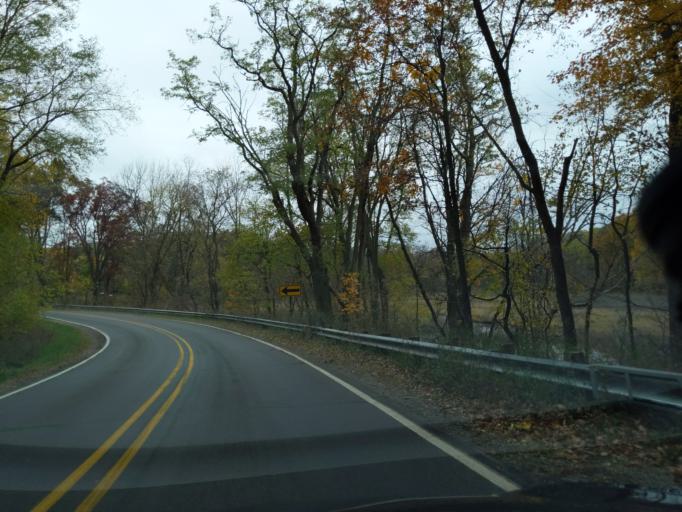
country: US
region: Michigan
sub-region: Jackson County
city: Spring Arbor
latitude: 42.3330
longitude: -84.6006
